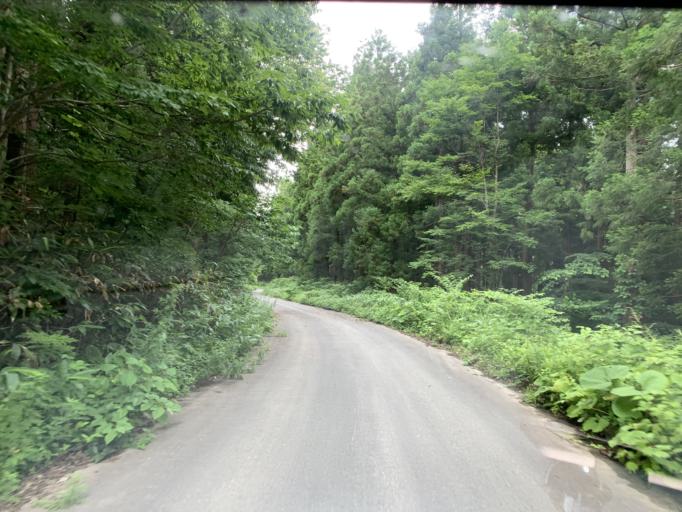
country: JP
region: Iwate
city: Ichinoseki
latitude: 38.9567
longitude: 140.8884
